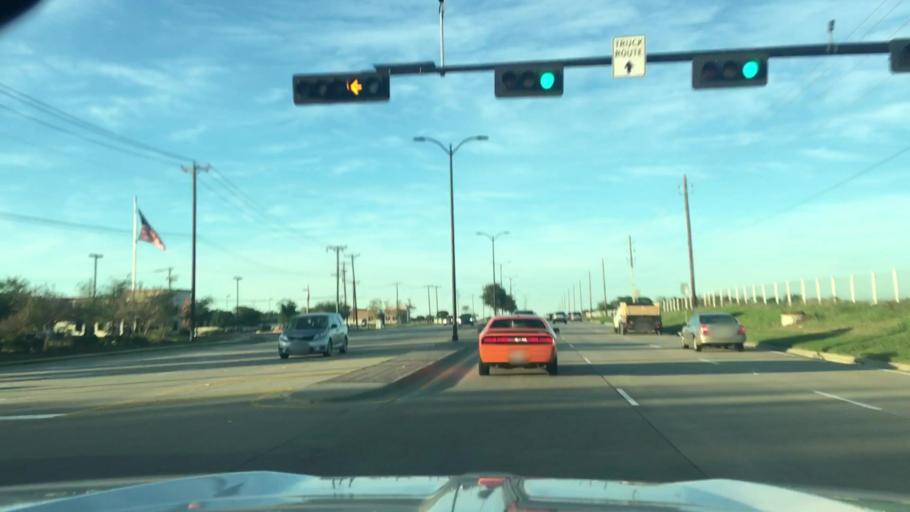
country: US
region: Texas
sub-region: Collin County
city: Frisco
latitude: 33.1633
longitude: -96.8031
